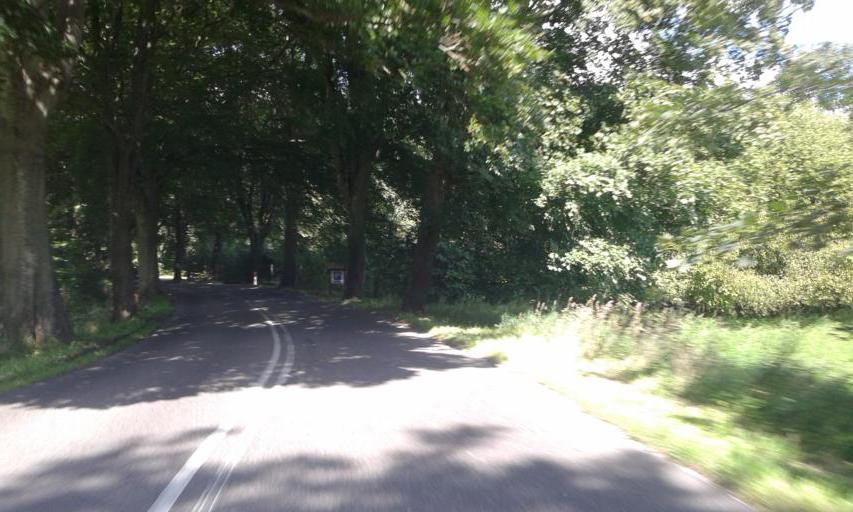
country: PL
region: West Pomeranian Voivodeship
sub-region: Powiat slawienski
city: Slawno
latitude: 54.2535
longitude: 16.6856
